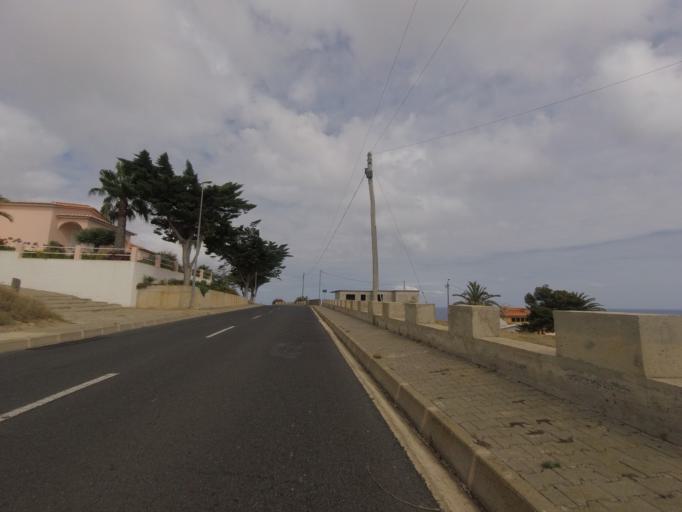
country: PT
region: Madeira
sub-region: Porto Santo
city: Vila de Porto Santo
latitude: 33.0540
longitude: -16.3461
